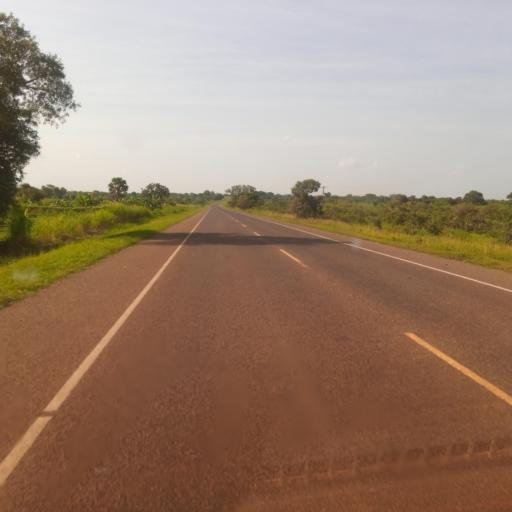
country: UG
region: Northern Region
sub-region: Kitgum District
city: Kitgum
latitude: 3.1593
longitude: 32.9162
